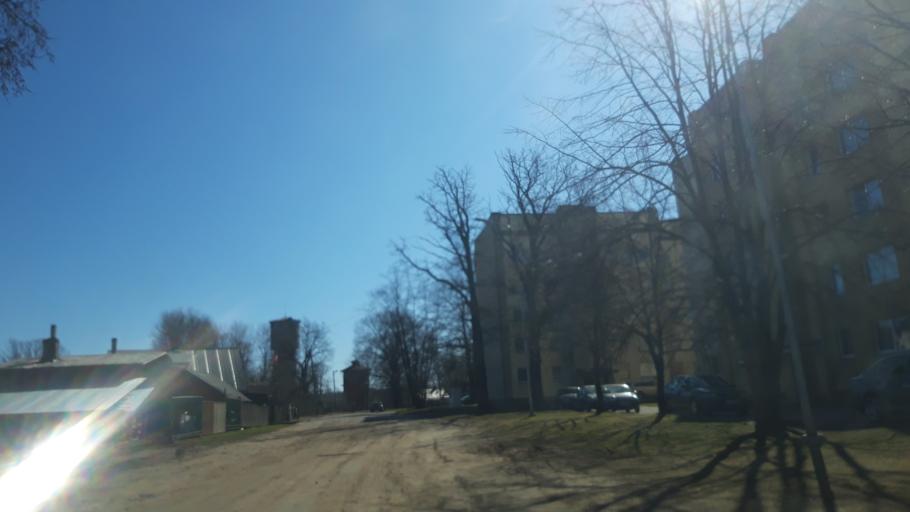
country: LV
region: Valmieras Rajons
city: Valmiera
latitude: 57.5250
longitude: 25.4393
